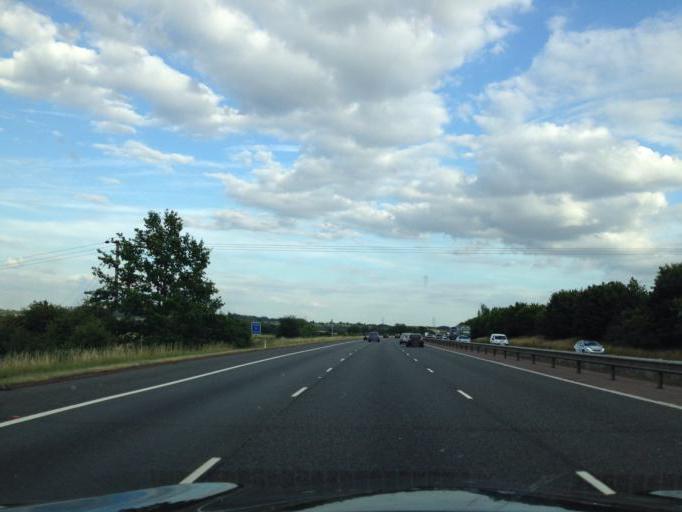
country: GB
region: England
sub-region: Oxfordshire
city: Bicester
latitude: 51.8408
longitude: -1.1403
